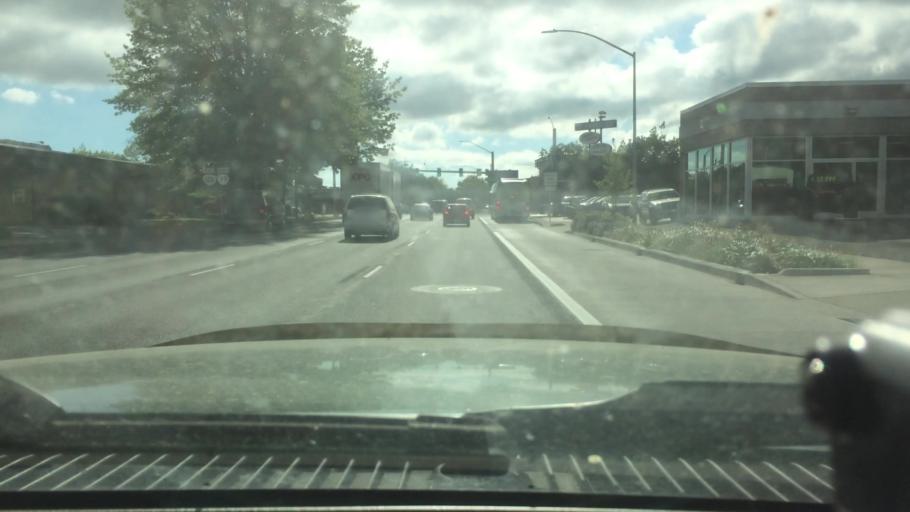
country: US
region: Oregon
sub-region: Lane County
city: Eugene
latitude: 44.0521
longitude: -123.1198
